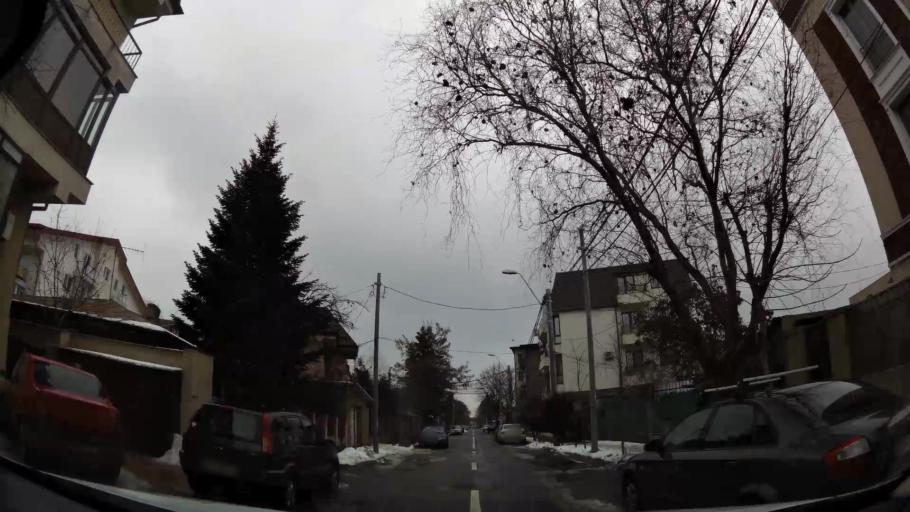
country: RO
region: Ilfov
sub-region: Comuna Chiajna
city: Rosu
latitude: 44.4877
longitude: 26.0298
